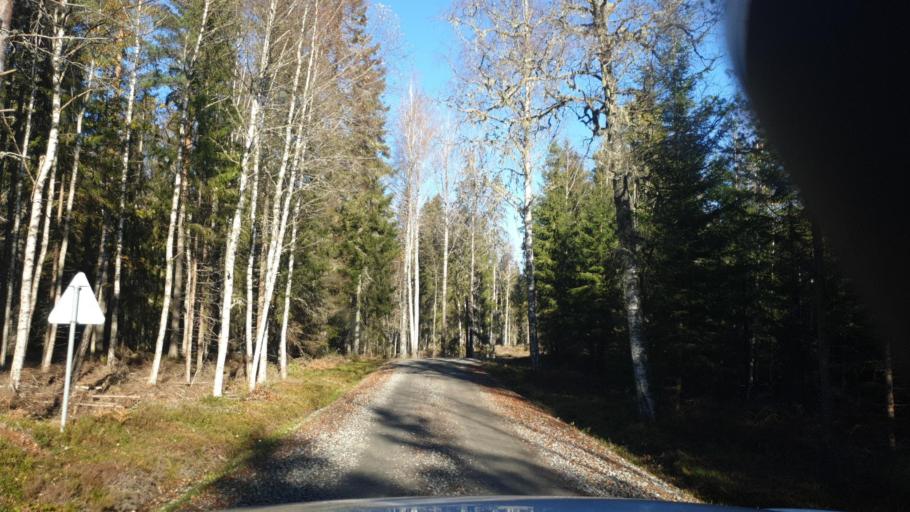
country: SE
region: Vaermland
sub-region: Karlstads Kommun
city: Valberg
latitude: 59.4529
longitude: 13.0942
